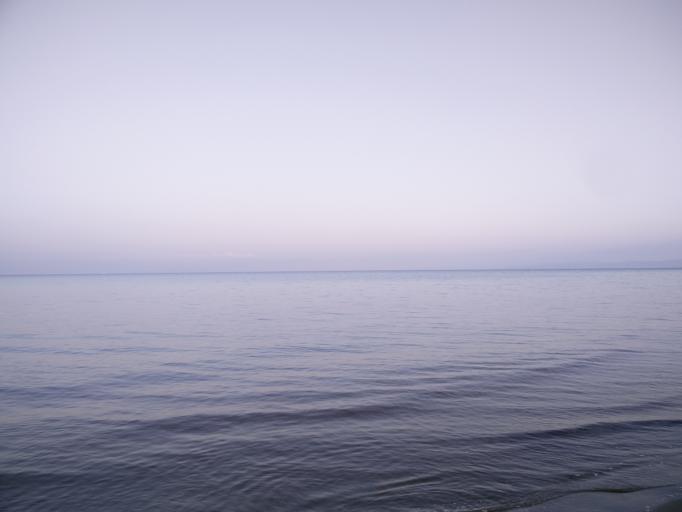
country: IT
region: Tuscany
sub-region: Provincia di Grosseto
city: Follonica
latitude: 42.8188
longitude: 10.7664
